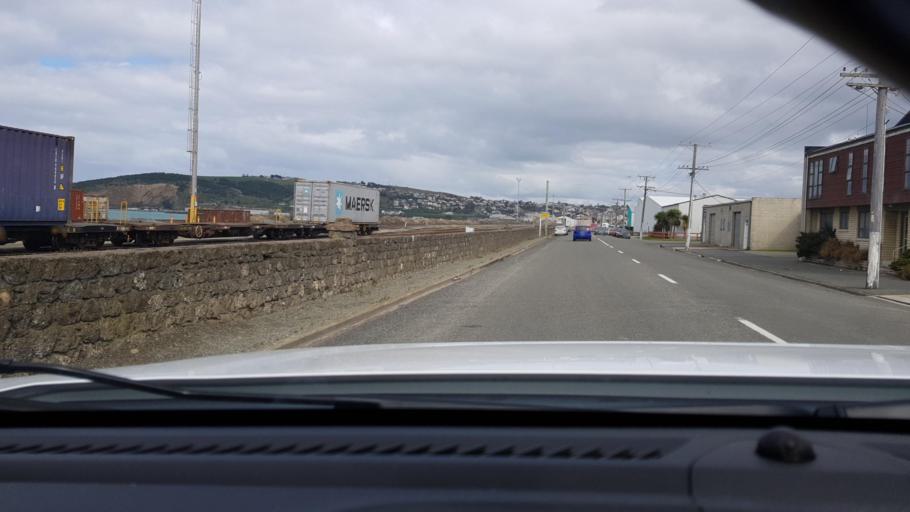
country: NZ
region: Otago
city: Oamaru
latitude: -45.0927
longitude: 170.9780
